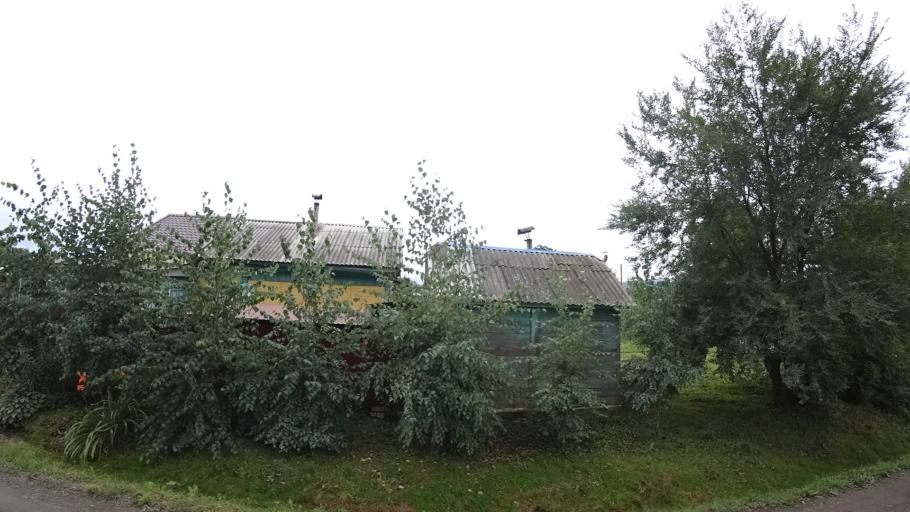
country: RU
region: Primorskiy
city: Chernigovka
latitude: 44.3371
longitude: 132.5723
